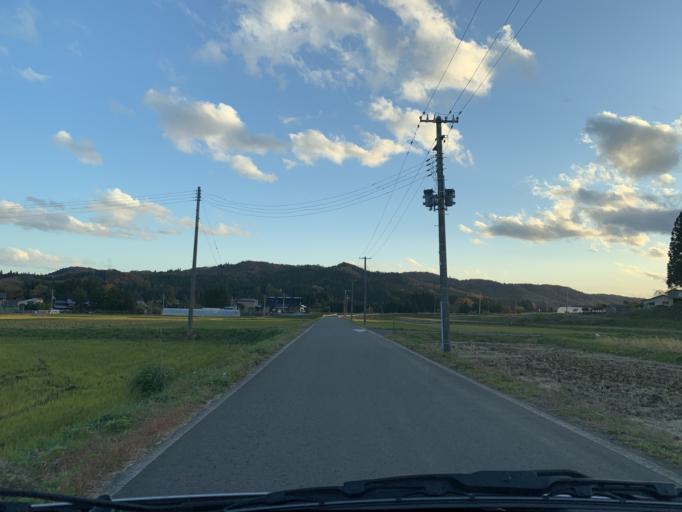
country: JP
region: Iwate
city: Mizusawa
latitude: 39.0385
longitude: 141.0556
